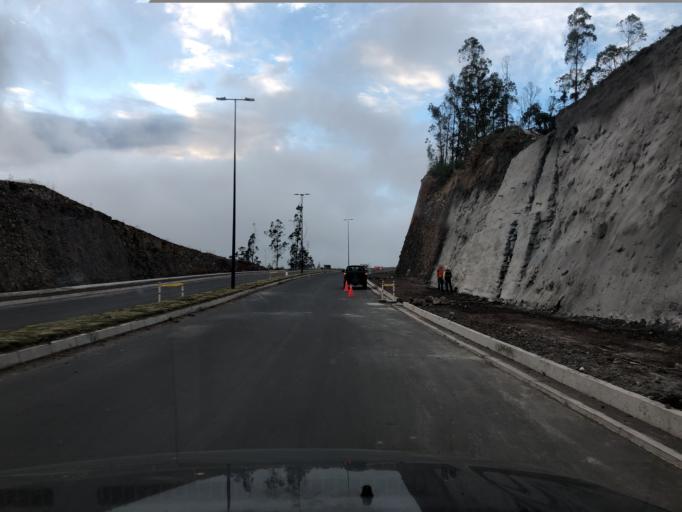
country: EC
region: Imbabura
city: Ibarra
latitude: 0.3579
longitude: -78.1394
